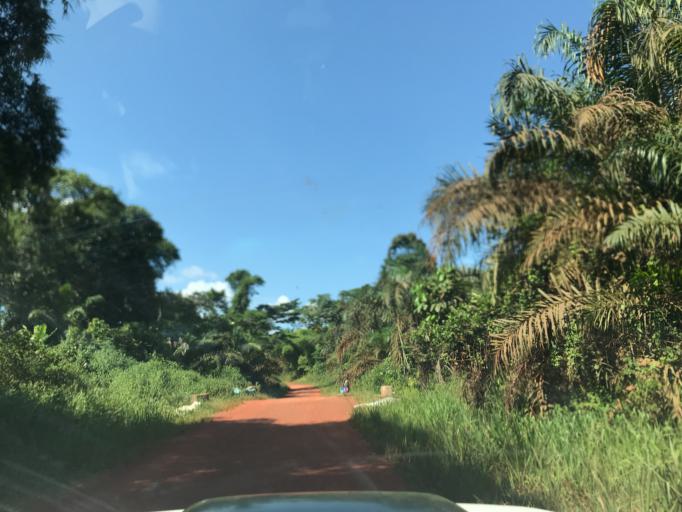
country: CD
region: Eastern Province
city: Kisangani
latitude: 1.2052
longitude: 25.2594
